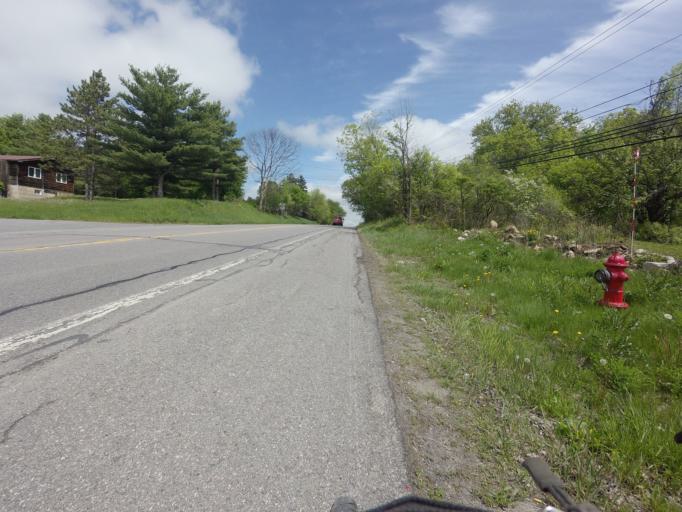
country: CA
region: Ontario
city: Cornwall
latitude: 44.9781
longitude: -74.6980
